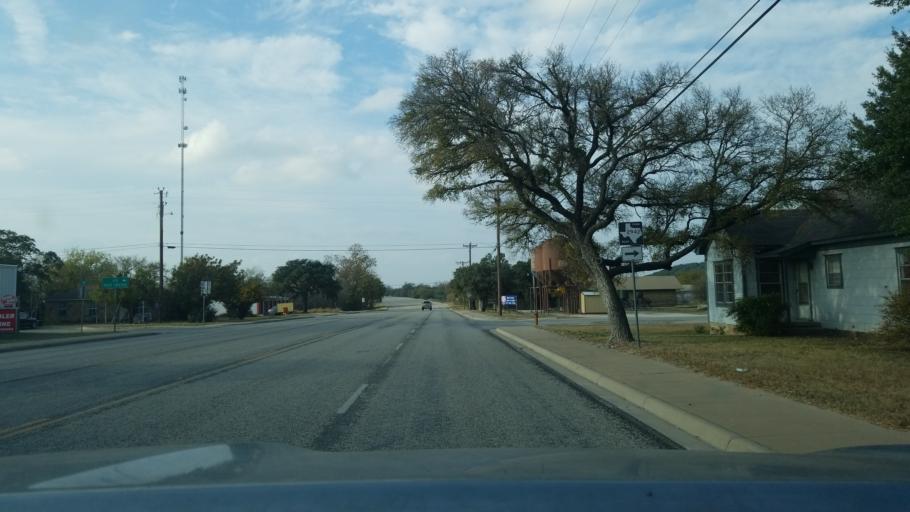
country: US
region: Texas
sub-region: Lampasas County
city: Lampasas
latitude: 31.2178
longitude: -98.3946
